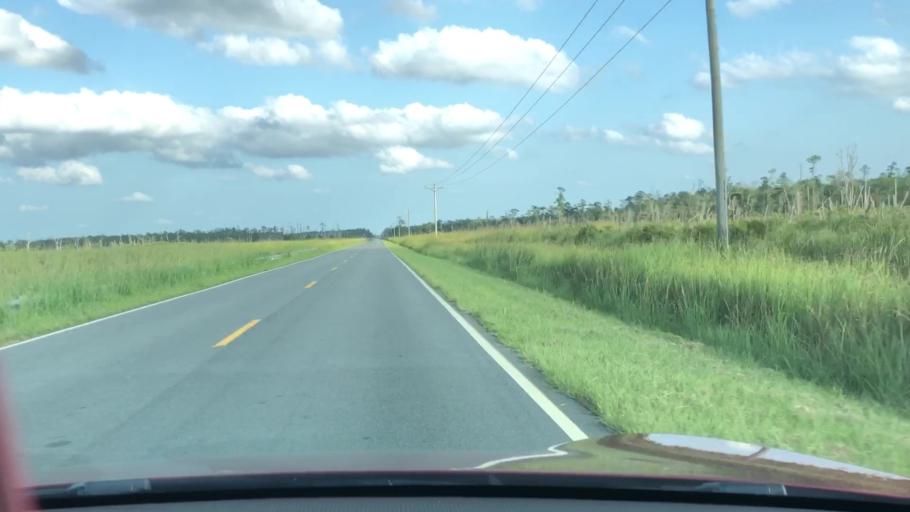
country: US
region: North Carolina
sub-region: Dare County
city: Wanchese
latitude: 35.6270
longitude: -75.8479
